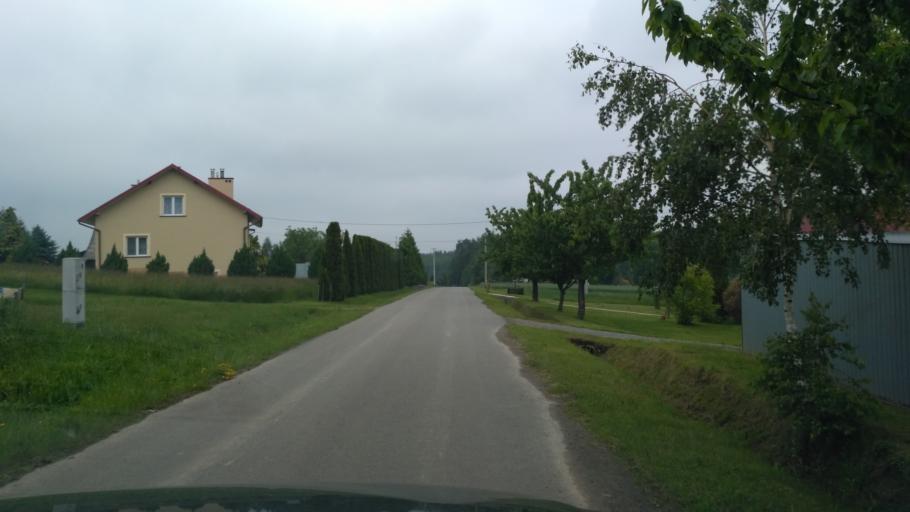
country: PL
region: Subcarpathian Voivodeship
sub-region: Powiat ropczycko-sedziszowski
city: Zagorzyce
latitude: 49.9885
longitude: 21.7060
